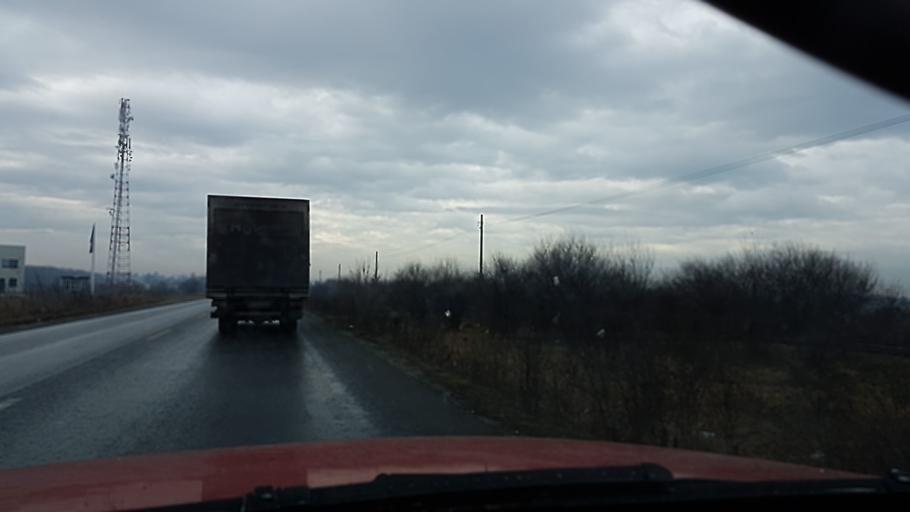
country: RO
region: Ilfov
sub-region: Comuna Glina
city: Catelu
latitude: 44.3682
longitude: 26.2114
